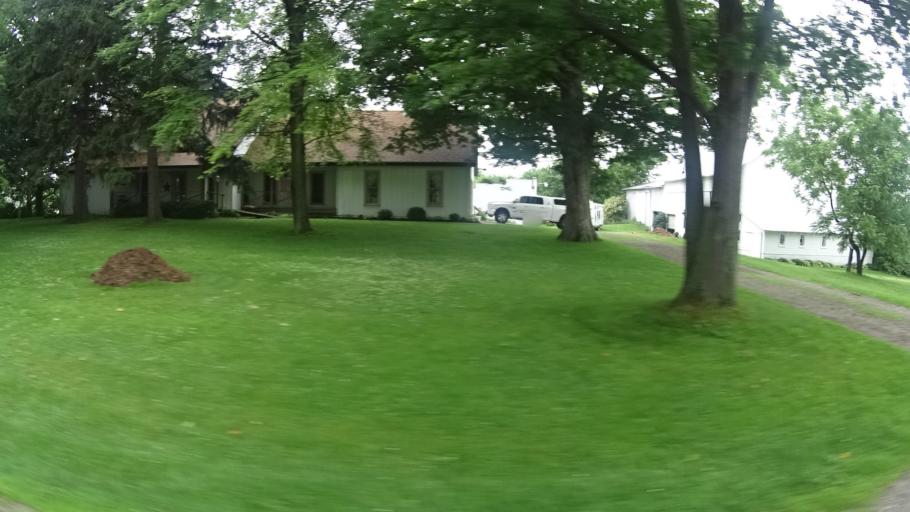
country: US
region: Ohio
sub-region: Erie County
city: Huron
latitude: 41.3569
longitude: -82.5754
